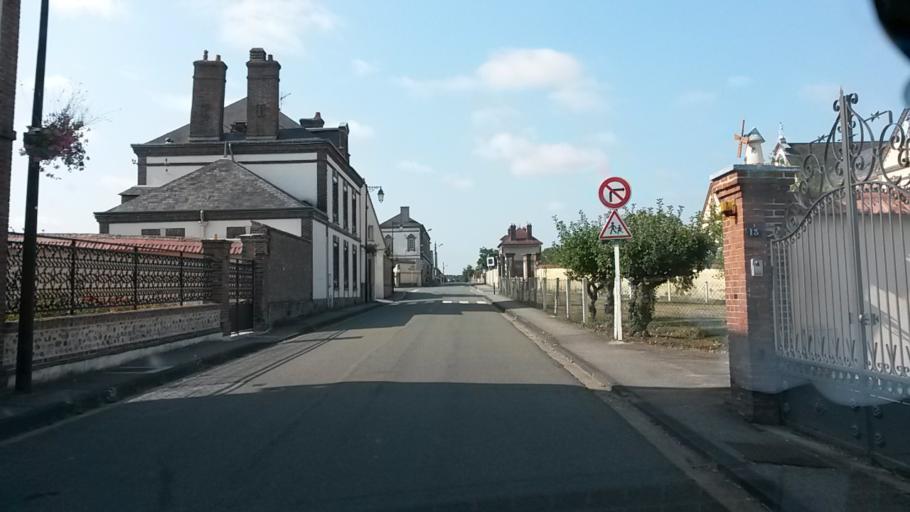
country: FR
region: Haute-Normandie
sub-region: Departement de l'Eure
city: Damville
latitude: 48.8681
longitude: 1.0726
